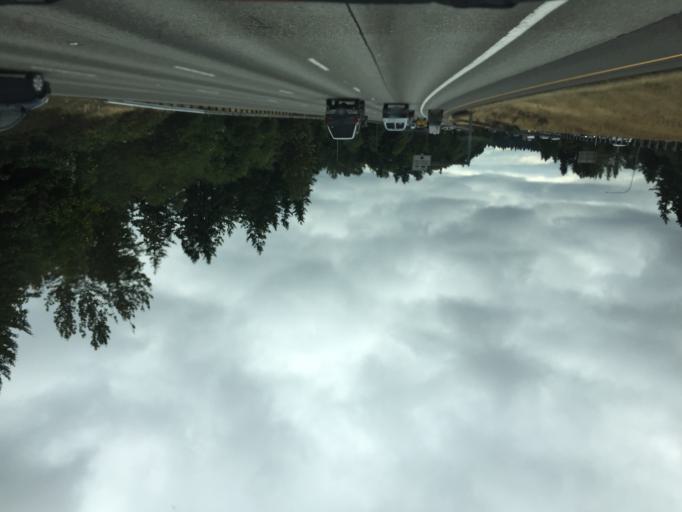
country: US
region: Washington
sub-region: King County
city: Lakeland North
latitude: 47.3550
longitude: -122.2968
